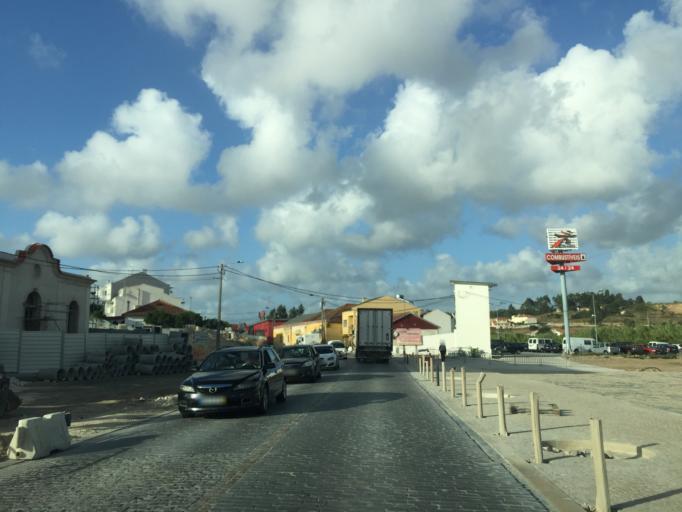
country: PT
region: Lisbon
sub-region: Torres Vedras
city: Torres Vedras
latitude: 39.1005
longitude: -9.2597
